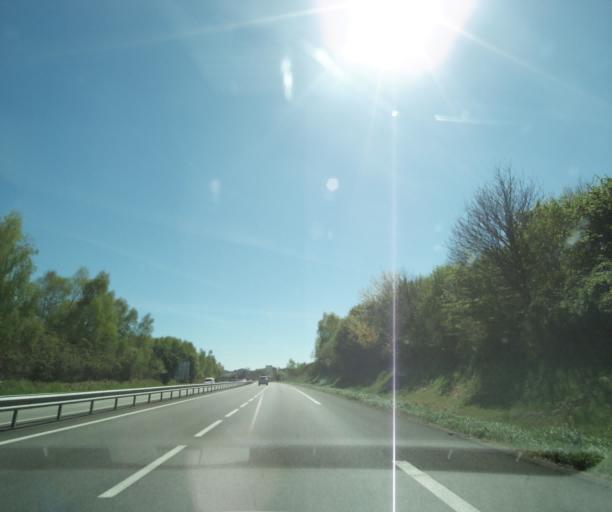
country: FR
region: Limousin
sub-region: Departement de la Haute-Vienne
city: Saint-Germain-les-Belles
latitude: 45.5321
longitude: 1.5121
